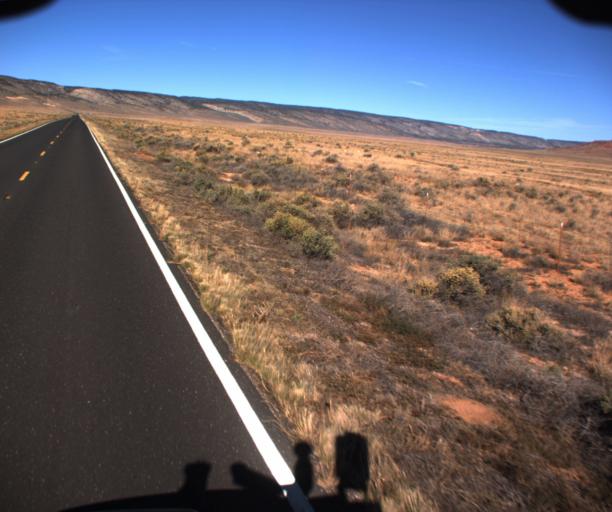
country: US
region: Arizona
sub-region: Coconino County
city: Fredonia
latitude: 36.7211
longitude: -112.0130
